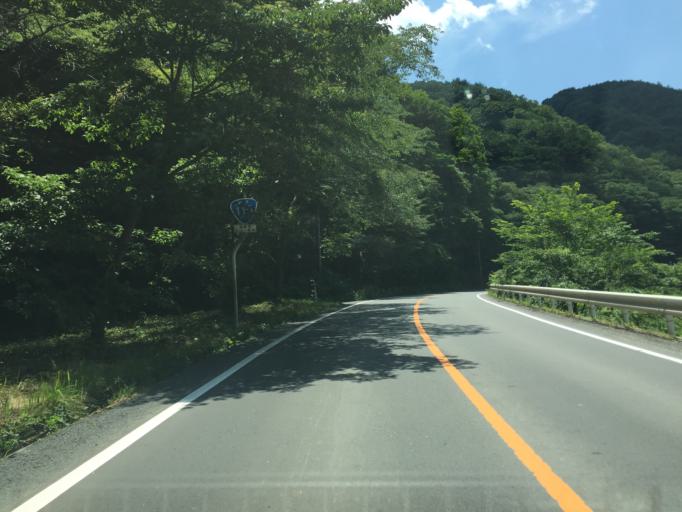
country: JP
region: Miyagi
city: Marumori
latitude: 37.7819
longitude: 140.8144
